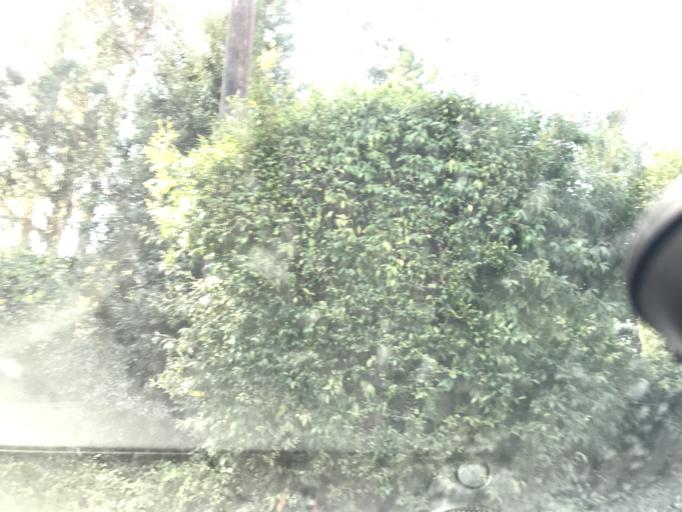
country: US
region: California
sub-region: Santa Barbara County
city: Goleta
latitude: 34.4530
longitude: -119.8009
